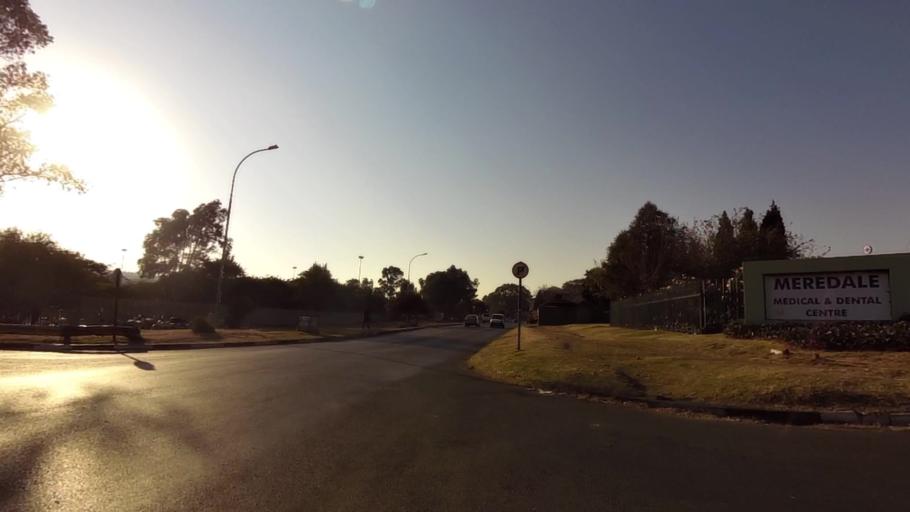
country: ZA
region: Gauteng
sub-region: City of Johannesburg Metropolitan Municipality
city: Soweto
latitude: -26.2758
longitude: 27.9609
